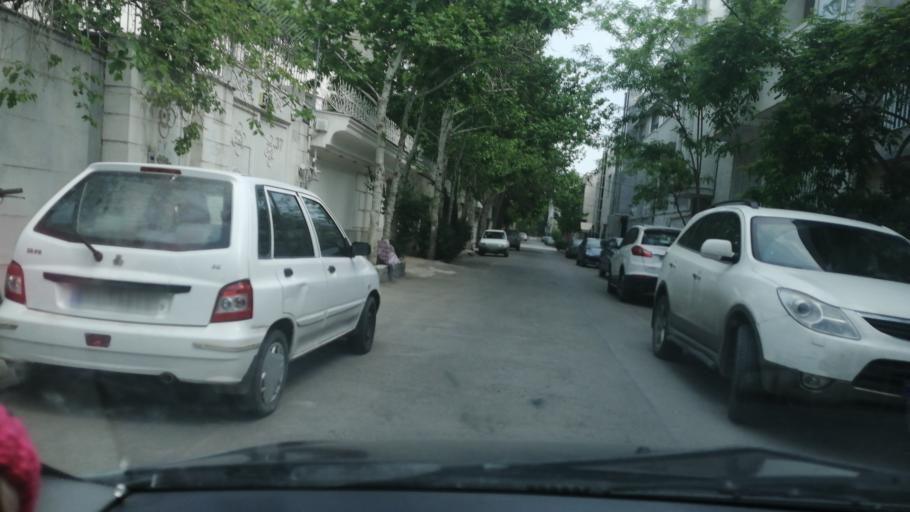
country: IR
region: Razavi Khorasan
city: Mashhad
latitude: 36.3080
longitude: 59.5542
